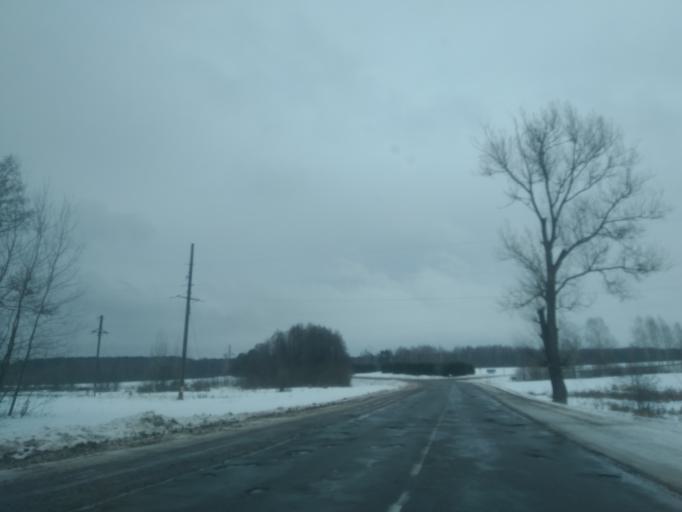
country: BY
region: Minsk
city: Ivyanyets
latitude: 53.9041
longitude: 26.7598
